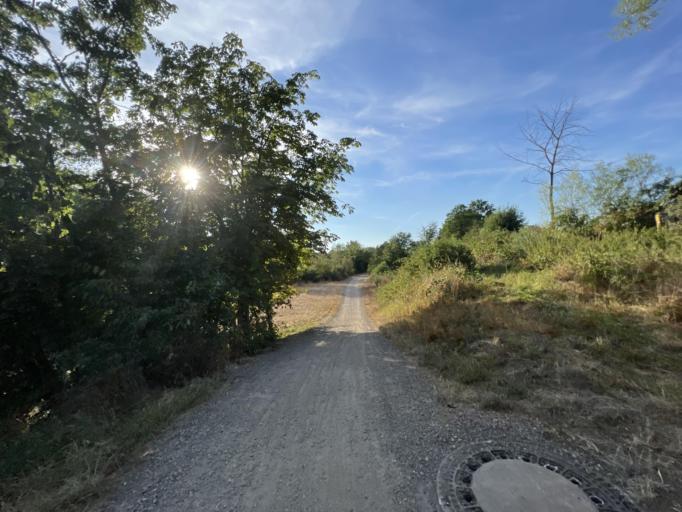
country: DE
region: North Rhine-Westphalia
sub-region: Regierungsbezirk Koln
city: Dueren
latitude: 50.8230
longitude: 6.4552
